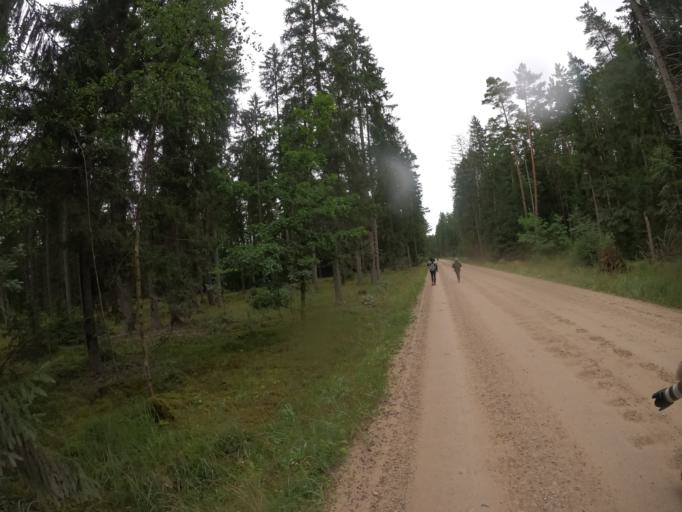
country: LV
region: Kuldigas Rajons
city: Kuldiga
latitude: 56.9971
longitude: 21.9790
